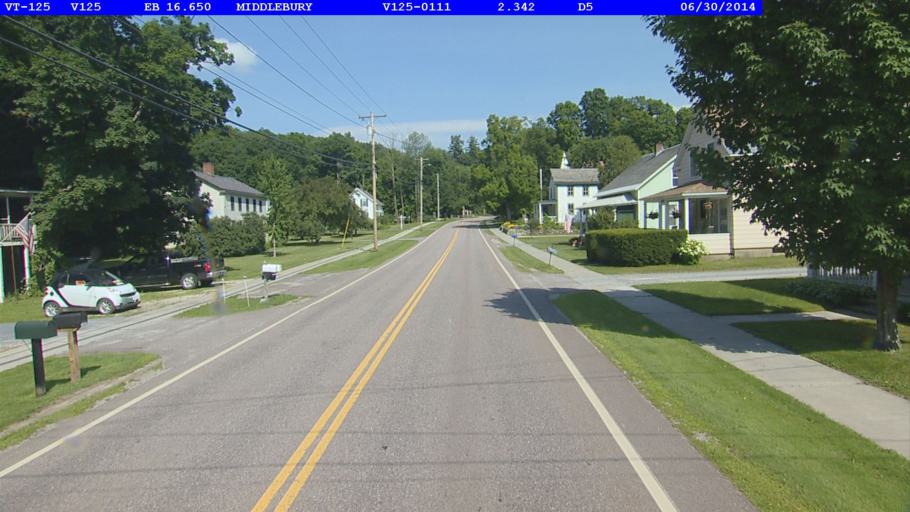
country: US
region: Vermont
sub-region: Addison County
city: Middlebury (village)
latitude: 43.9718
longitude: -73.0949
